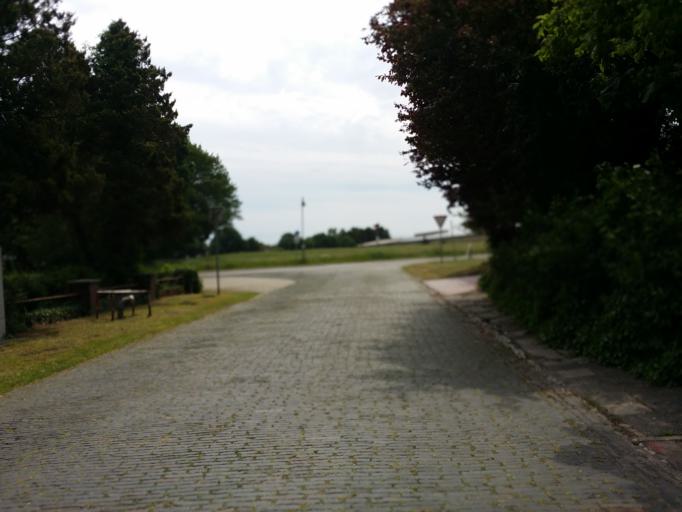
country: DE
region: Lower Saxony
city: Bockhorn
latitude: 53.3680
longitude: 7.9949
